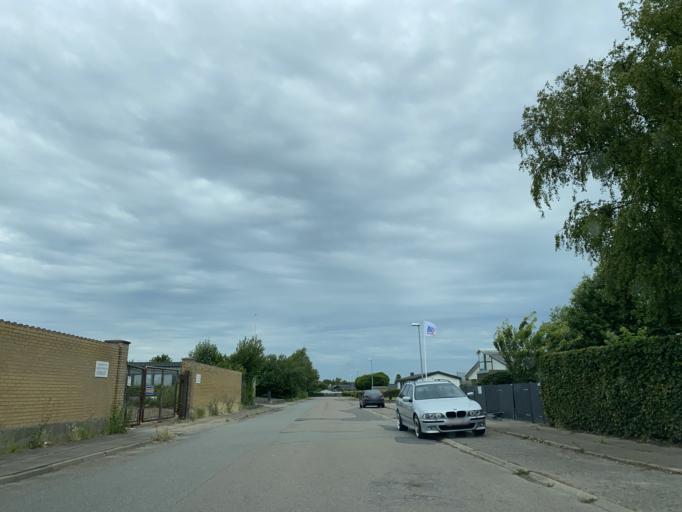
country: DK
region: South Denmark
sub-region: Sonderborg Kommune
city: Sonderborg
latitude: 54.9232
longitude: 9.8160
